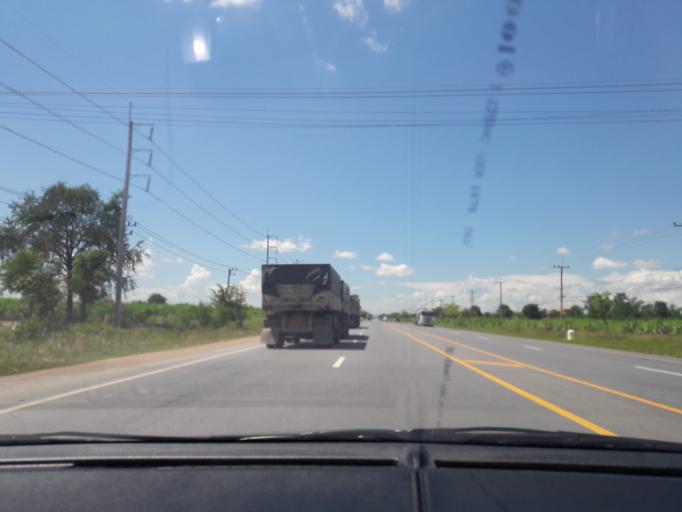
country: TH
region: Kanchanaburi
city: Phanom Thuan
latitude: 14.0521
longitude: 99.7766
